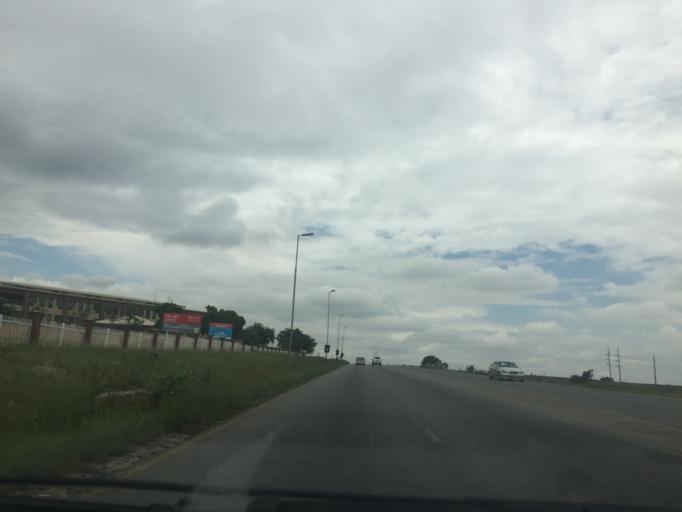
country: ZA
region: Gauteng
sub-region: City of Johannesburg Metropolitan Municipality
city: Midrand
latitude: -26.0097
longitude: 28.1330
